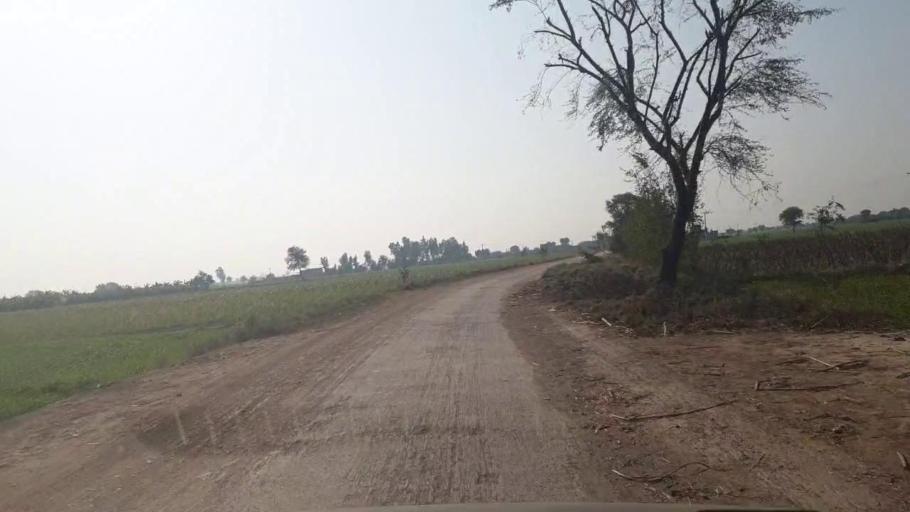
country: PK
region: Sindh
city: Bhit Shah
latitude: 25.7507
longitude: 68.5619
